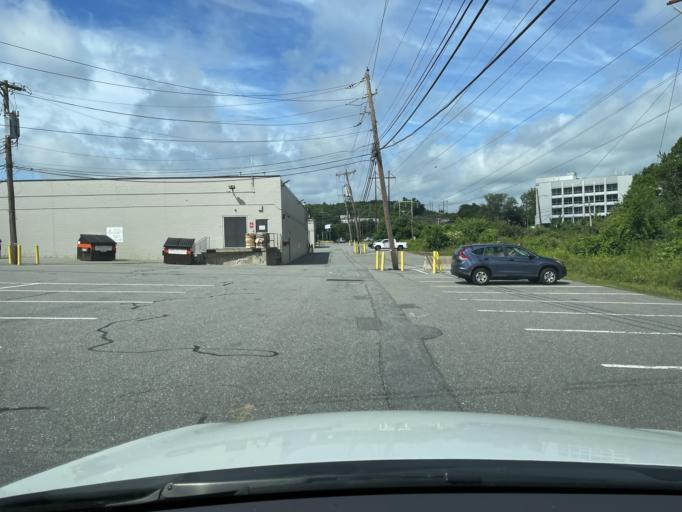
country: US
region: Massachusetts
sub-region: Middlesex County
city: Woburn
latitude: 42.4616
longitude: -71.1640
